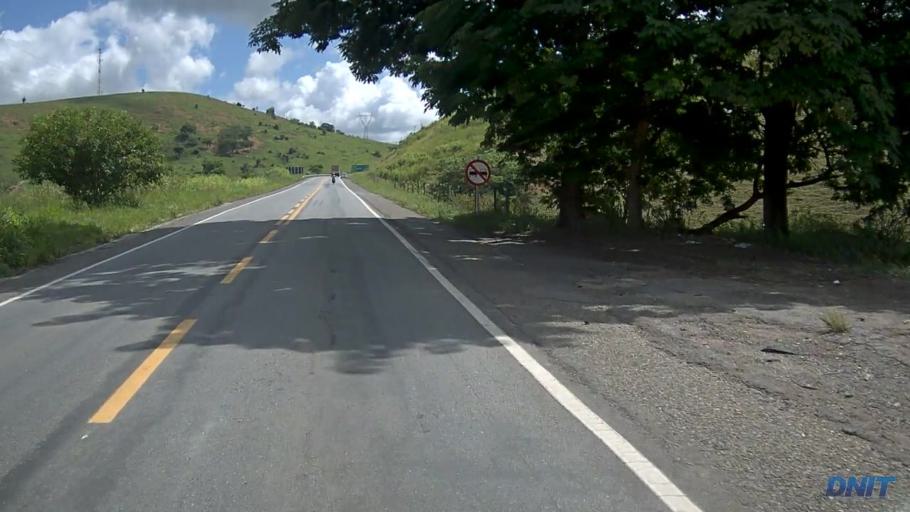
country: BR
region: Minas Gerais
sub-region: Governador Valadares
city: Governador Valadares
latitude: -19.0266
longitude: -42.1470
